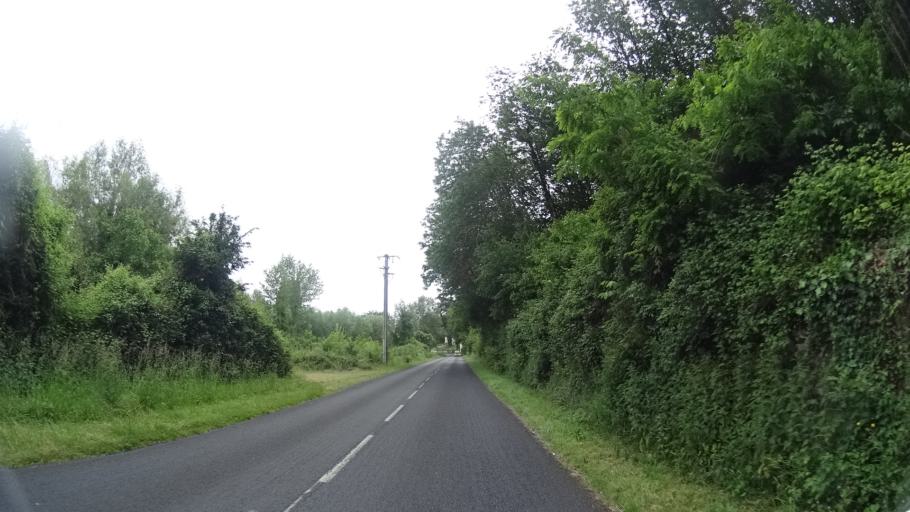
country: FR
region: Pays de la Loire
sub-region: Departement de Maine-et-Loire
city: Gennes
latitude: 47.3381
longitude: -0.2196
